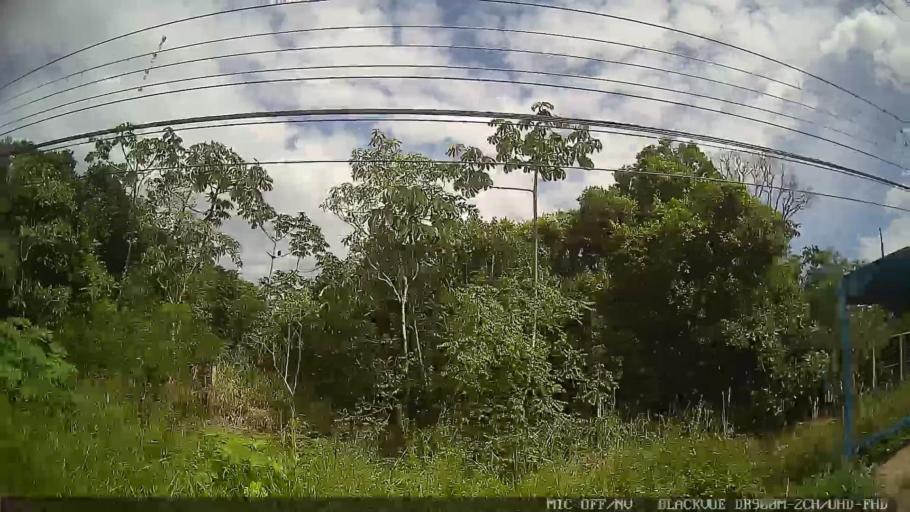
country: BR
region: Sao Paulo
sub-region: Mogi das Cruzes
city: Mogi das Cruzes
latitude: -23.5820
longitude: -46.2257
